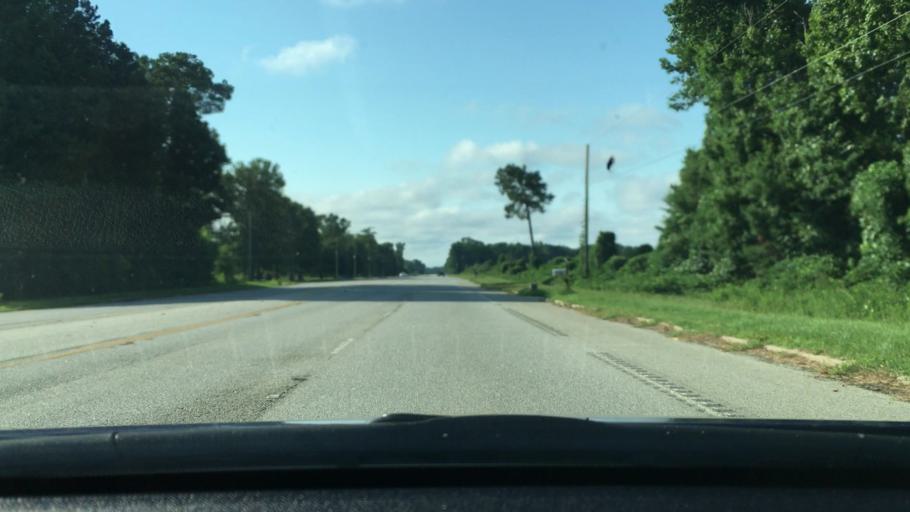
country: US
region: South Carolina
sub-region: Clarendon County
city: Manning
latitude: 33.7667
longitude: -80.2334
